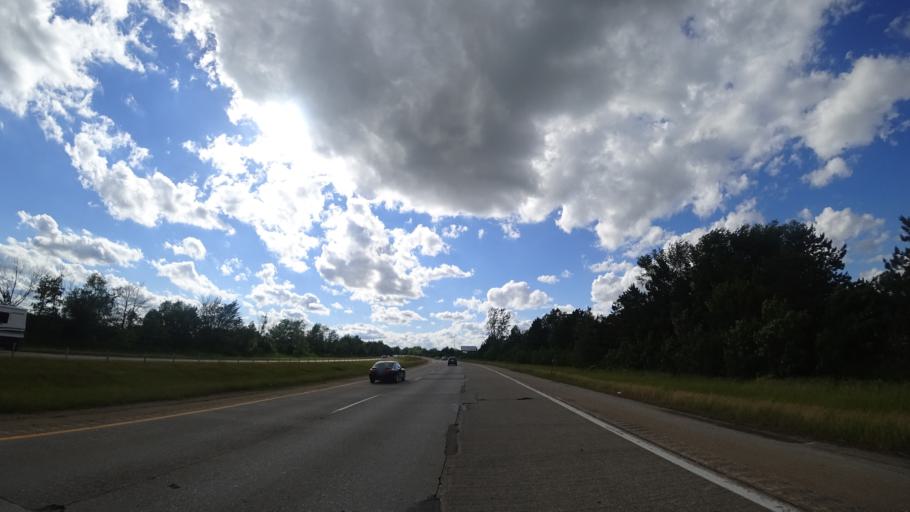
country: US
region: Michigan
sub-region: Ionia County
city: Portland
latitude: 42.8758
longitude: -84.9680
